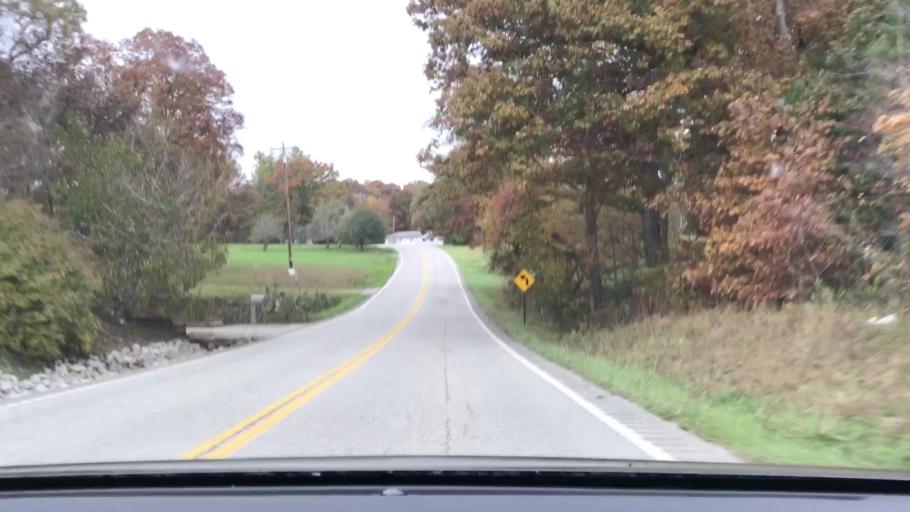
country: US
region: Tennessee
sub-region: Scott County
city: Huntsville
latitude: 36.3473
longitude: -84.6588
